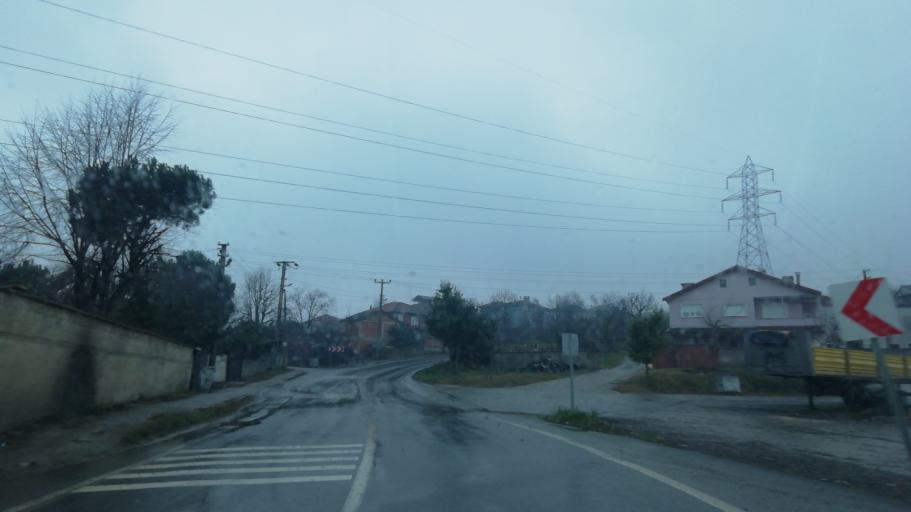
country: TR
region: Sakarya
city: Karapurcek
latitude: 40.6884
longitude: 30.5093
